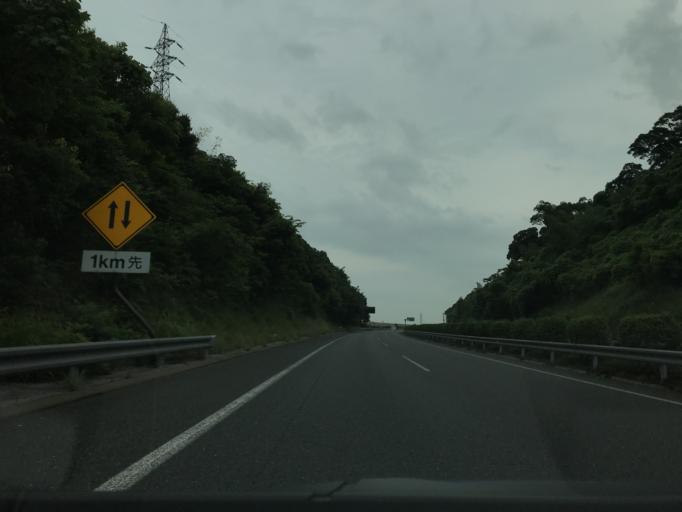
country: JP
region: Fukuoka
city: Kanda
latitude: 33.7992
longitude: 130.9573
